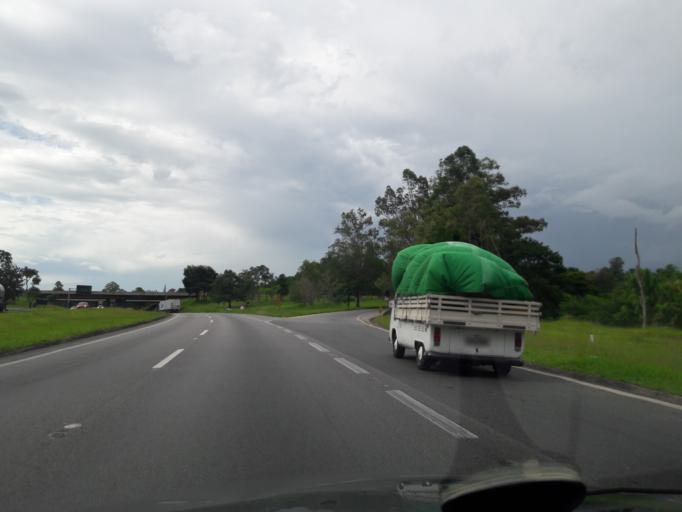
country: BR
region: Sao Paulo
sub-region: Atibaia
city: Atibaia
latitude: -23.1026
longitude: -46.5684
